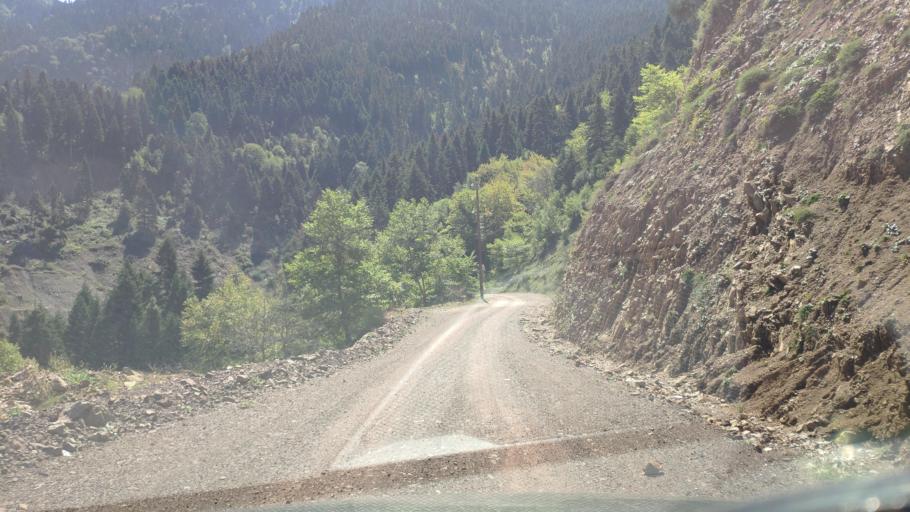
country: GR
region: Central Greece
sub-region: Nomos Evrytanias
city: Kerasochori
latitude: 39.1149
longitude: 21.6208
